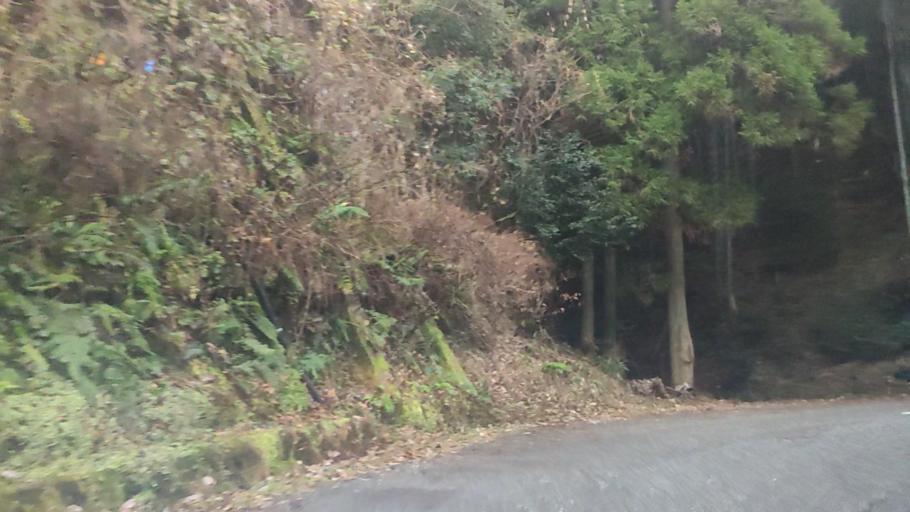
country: JP
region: Kumamoto
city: Matsubase
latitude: 32.5916
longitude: 130.8849
